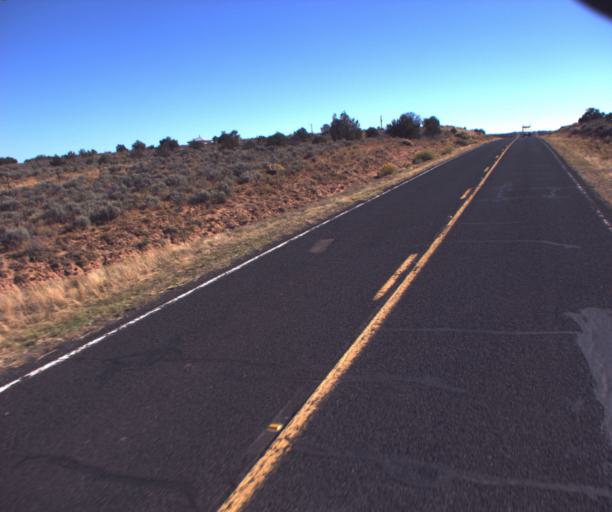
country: US
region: Arizona
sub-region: Apache County
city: Ganado
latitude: 35.6616
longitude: -109.5494
